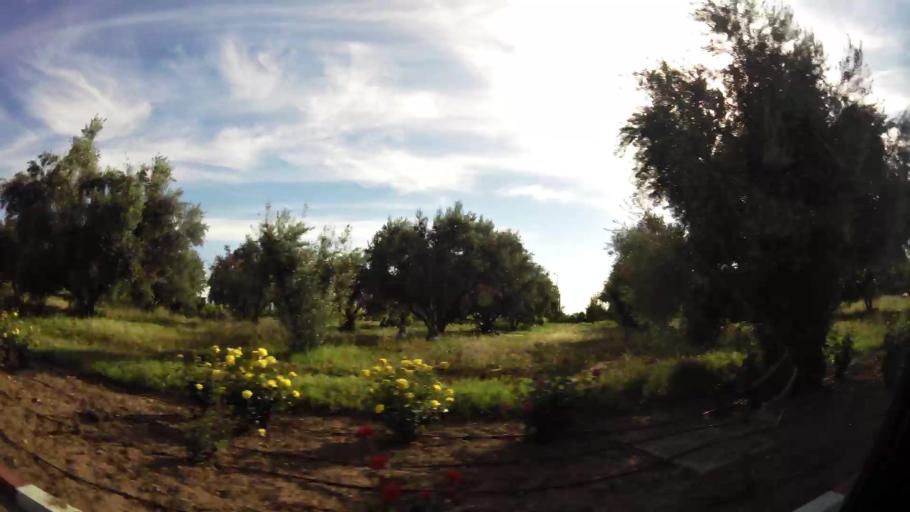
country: MA
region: Marrakech-Tensift-Al Haouz
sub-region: Marrakech
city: Marrakesh
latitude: 31.6153
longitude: -8.0046
